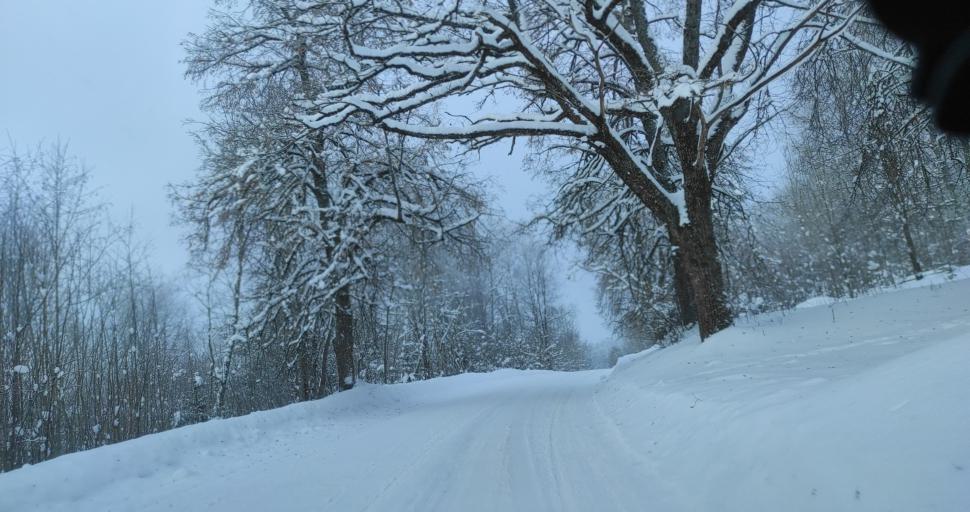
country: LV
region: Madonas Rajons
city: Madona
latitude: 56.8698
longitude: 25.9816
